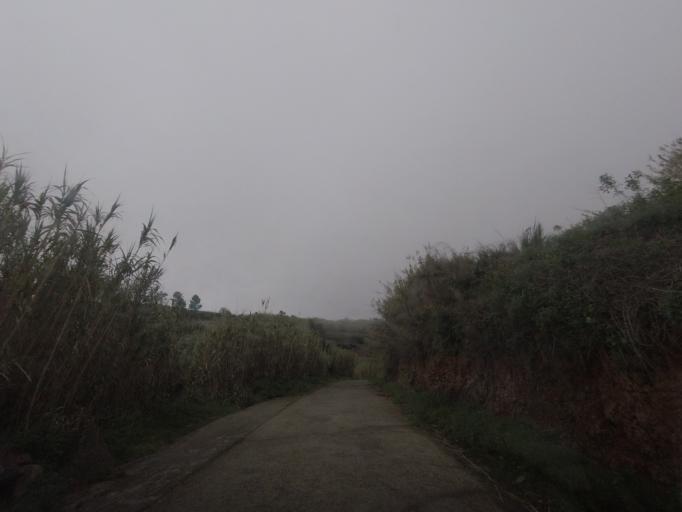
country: PT
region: Madeira
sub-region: Calheta
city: Faja da Ovelha
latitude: 32.7596
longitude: -17.2197
